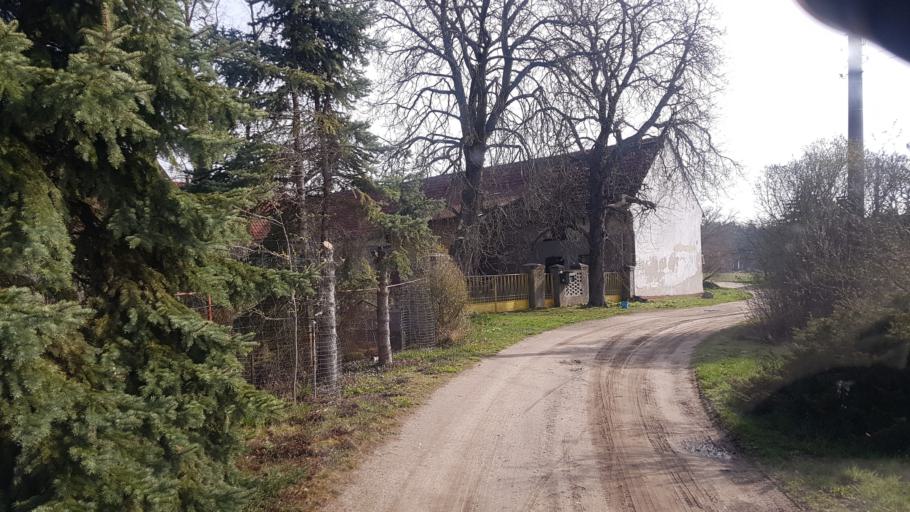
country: DE
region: Brandenburg
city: Schonborn
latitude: 51.6804
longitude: 13.4822
